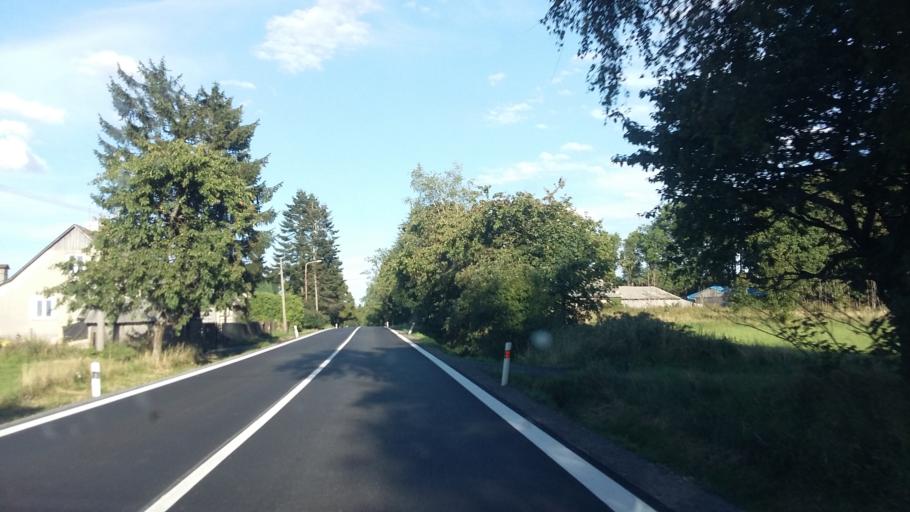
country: CZ
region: Central Bohemia
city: Rozmital pod Tremsinem
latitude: 49.6226
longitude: 13.7536
